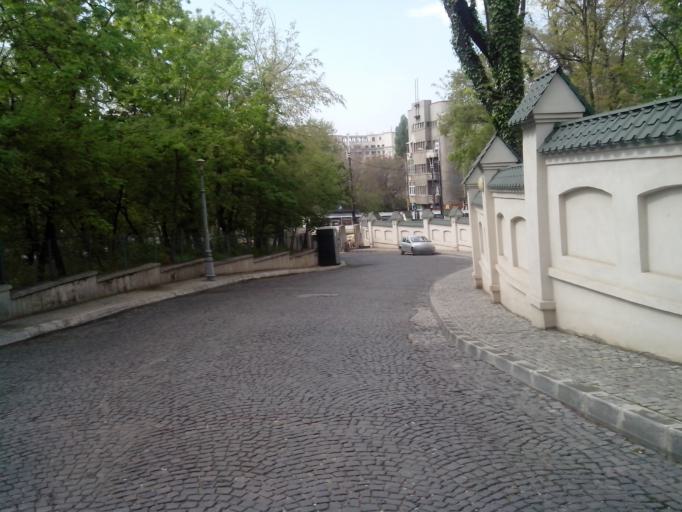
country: RO
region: Bucuresti
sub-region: Municipiul Bucuresti
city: Bucuresti
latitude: 44.4236
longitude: 26.0961
